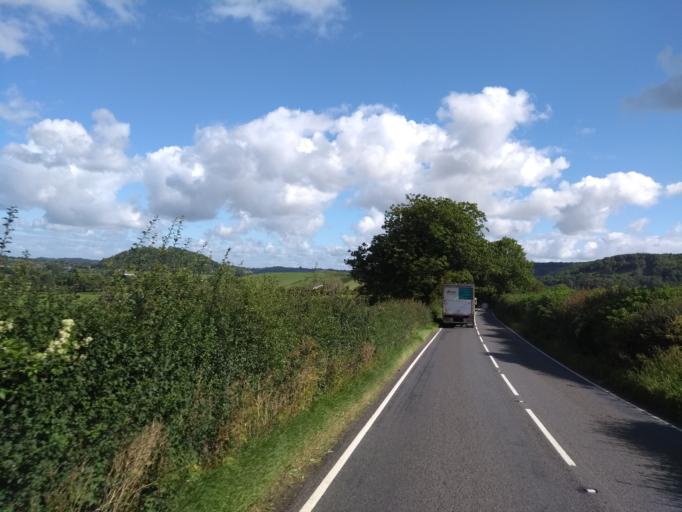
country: GB
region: England
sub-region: Somerset
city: Street
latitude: 51.0678
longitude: -2.7280
